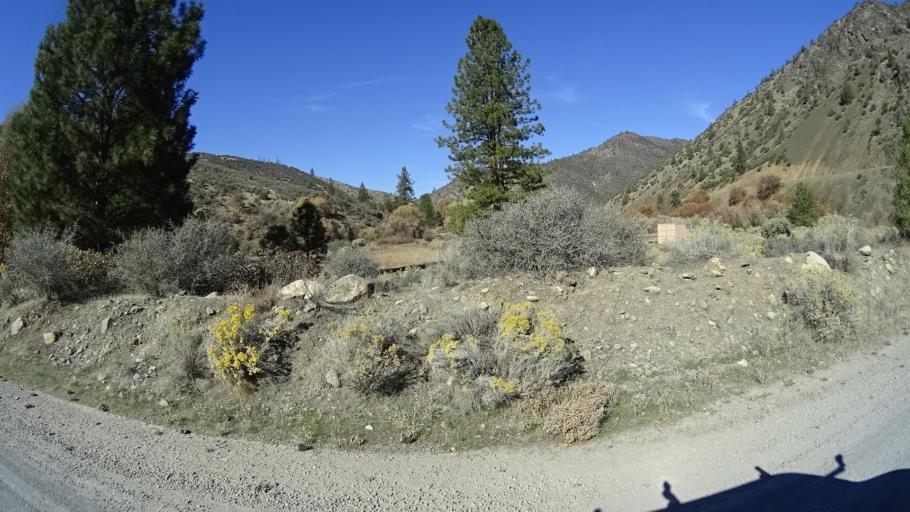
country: US
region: California
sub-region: Siskiyou County
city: Yreka
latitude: 41.8326
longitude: -122.6655
